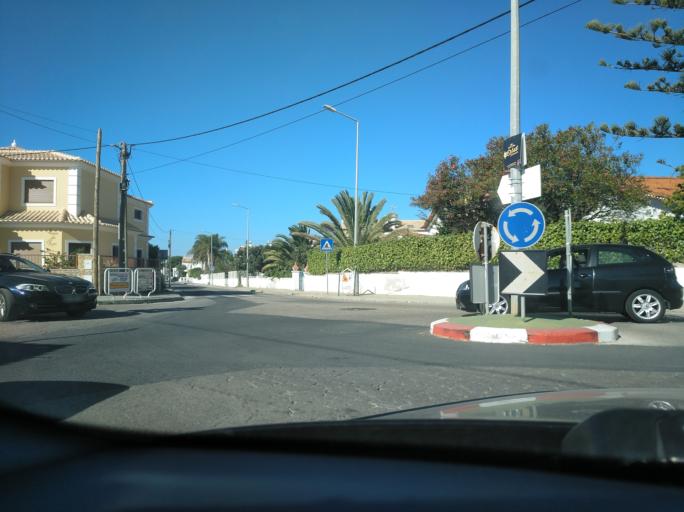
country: PT
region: Faro
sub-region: Vila Real de Santo Antonio
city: Monte Gordo
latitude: 37.1701
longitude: -7.5177
